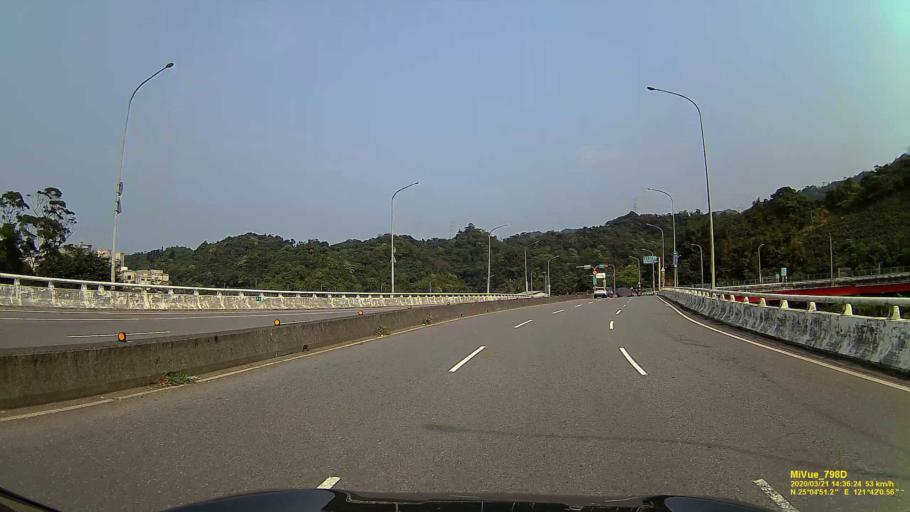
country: TW
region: Taiwan
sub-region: Keelung
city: Keelung
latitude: 25.0810
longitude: 121.7001
